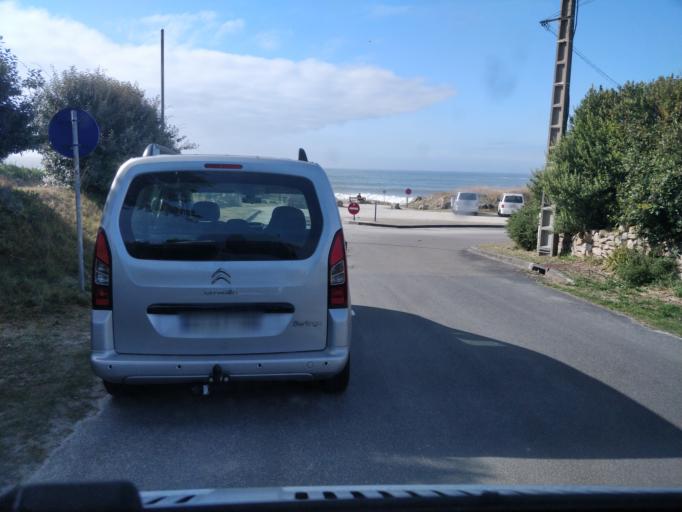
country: FR
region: Brittany
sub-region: Departement du Finistere
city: Plouhinec
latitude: 48.0021
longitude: -4.4981
